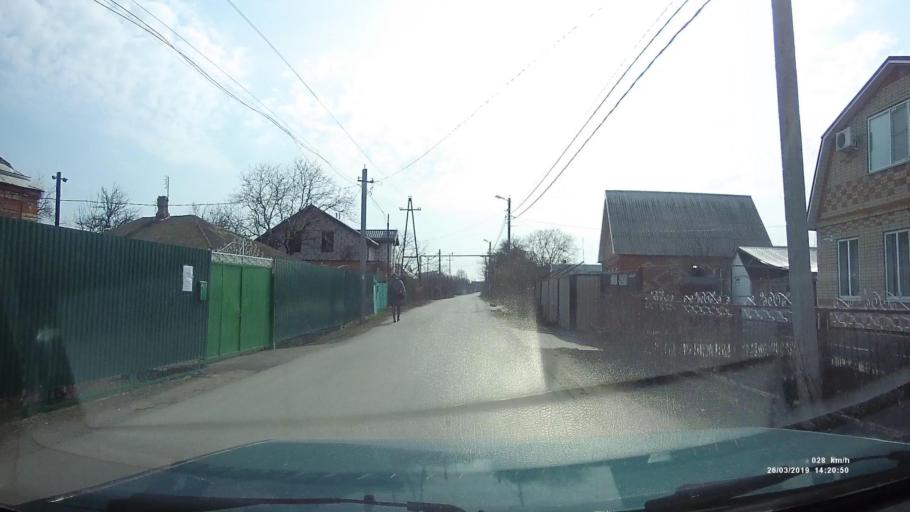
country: RU
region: Rostov
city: Novobessergenovka
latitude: 47.1887
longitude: 38.8701
